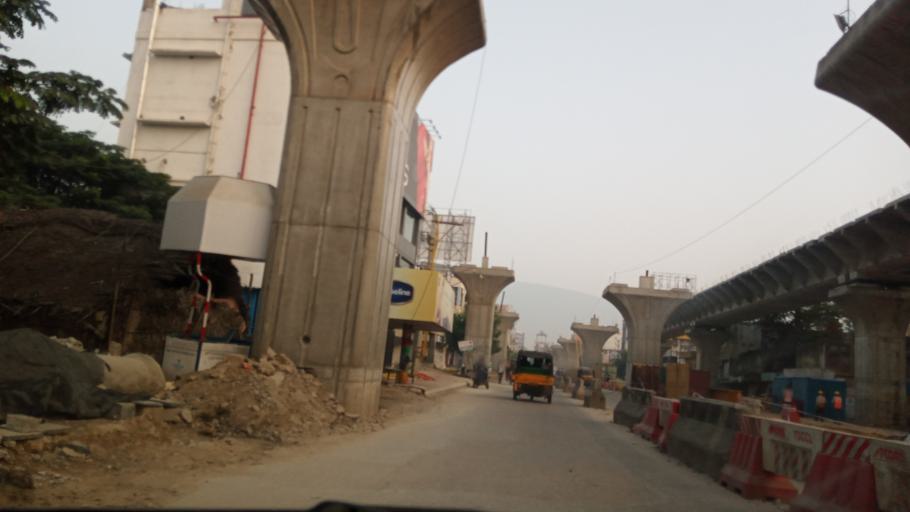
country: IN
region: Andhra Pradesh
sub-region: Chittoor
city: Tirupati
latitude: 13.6350
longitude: 79.4278
